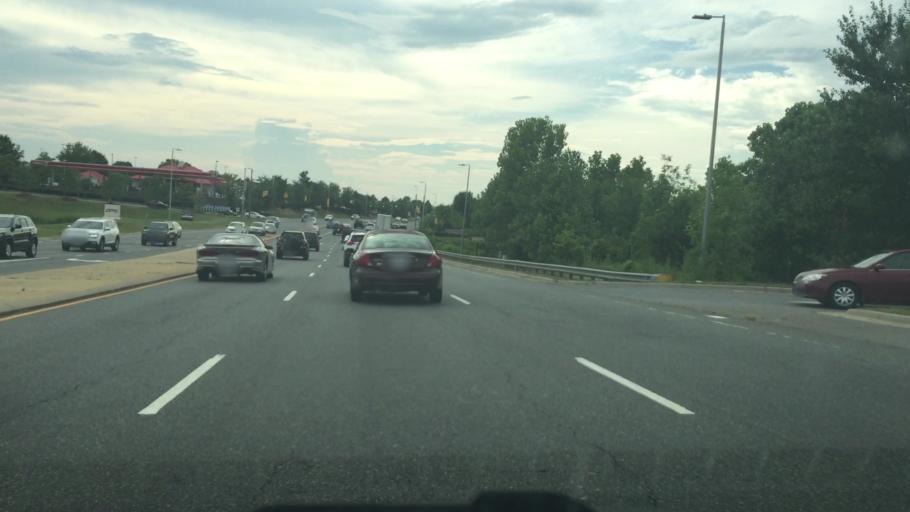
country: US
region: North Carolina
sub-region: Cabarrus County
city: Harrisburg
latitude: 35.3717
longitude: -80.7189
